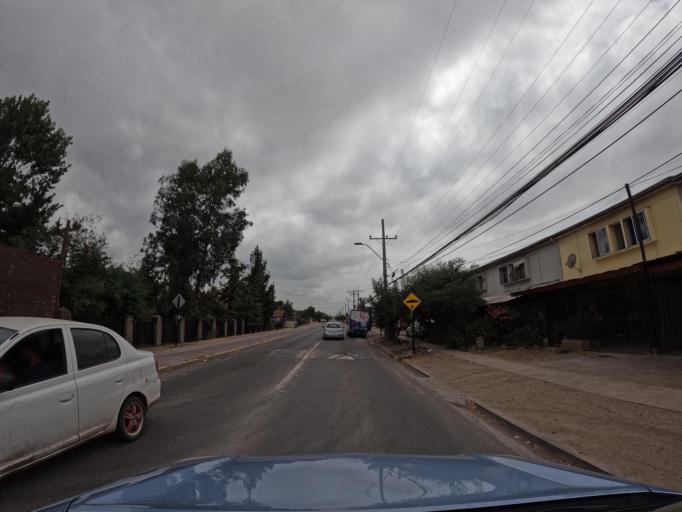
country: CL
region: O'Higgins
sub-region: Provincia de Colchagua
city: Chimbarongo
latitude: -34.7160
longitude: -71.0488
